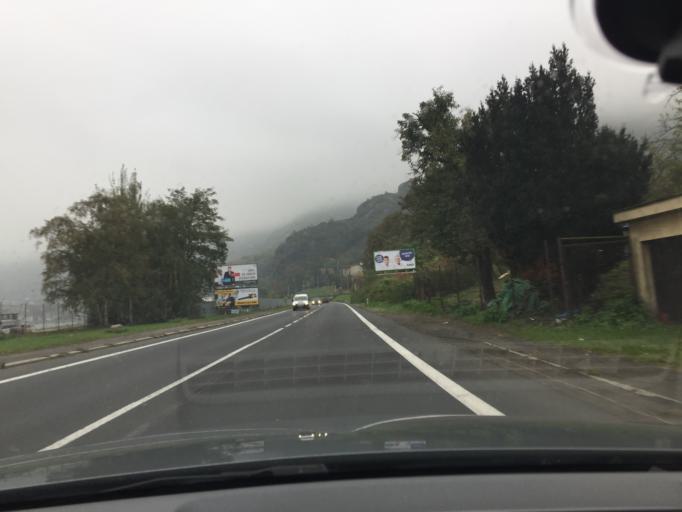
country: CZ
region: Ustecky
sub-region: Okres Usti nad Labem
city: Usti nad Labem
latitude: 50.6360
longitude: 14.0471
